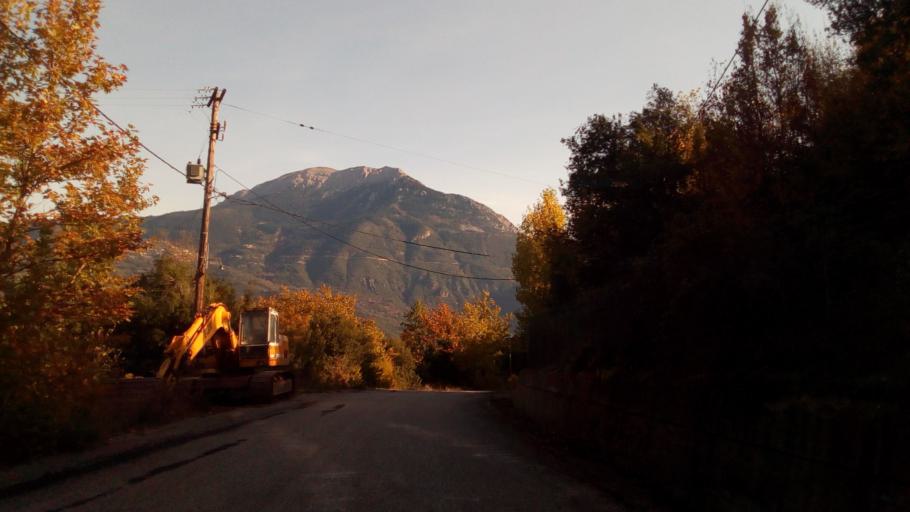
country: GR
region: West Greece
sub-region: Nomos Aitolias kai Akarnanias
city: Thermo
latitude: 38.6544
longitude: 21.8518
